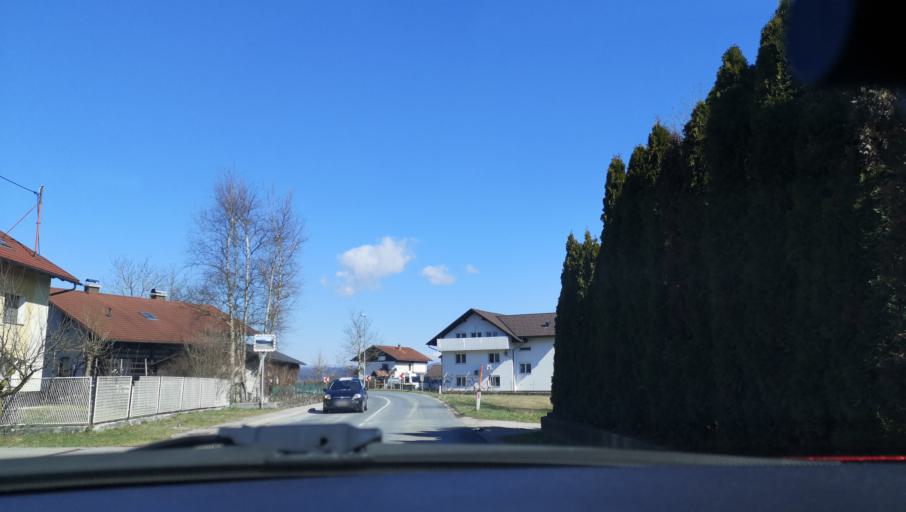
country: SI
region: Ig
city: Ig
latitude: 45.9601
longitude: 14.5309
